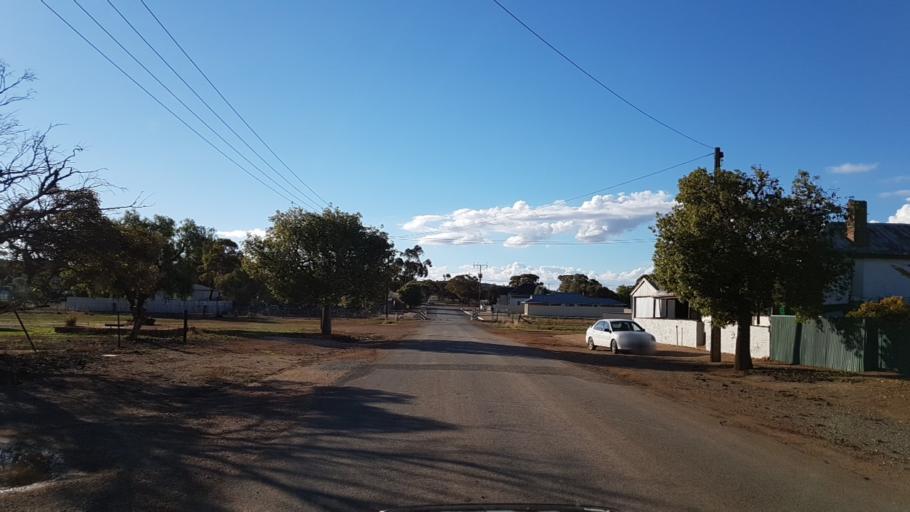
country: AU
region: South Australia
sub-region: Peterborough
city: Peterborough
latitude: -32.9717
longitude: 138.8407
